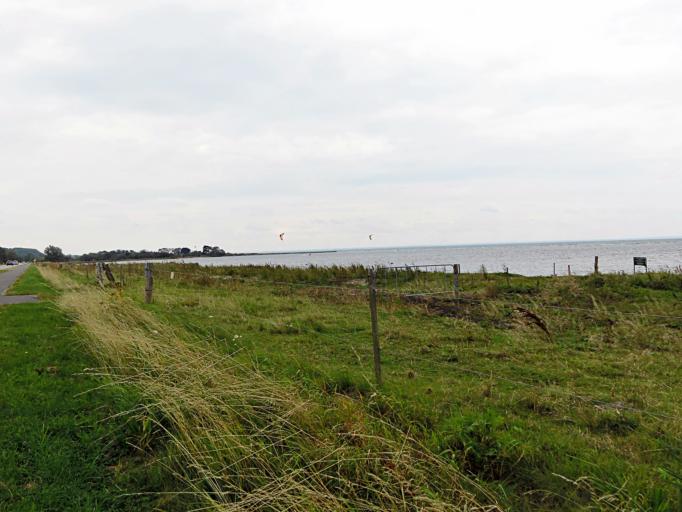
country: DK
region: Capital Region
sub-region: Fredensborg Kommune
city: Niva
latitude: 55.9317
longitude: 12.5208
